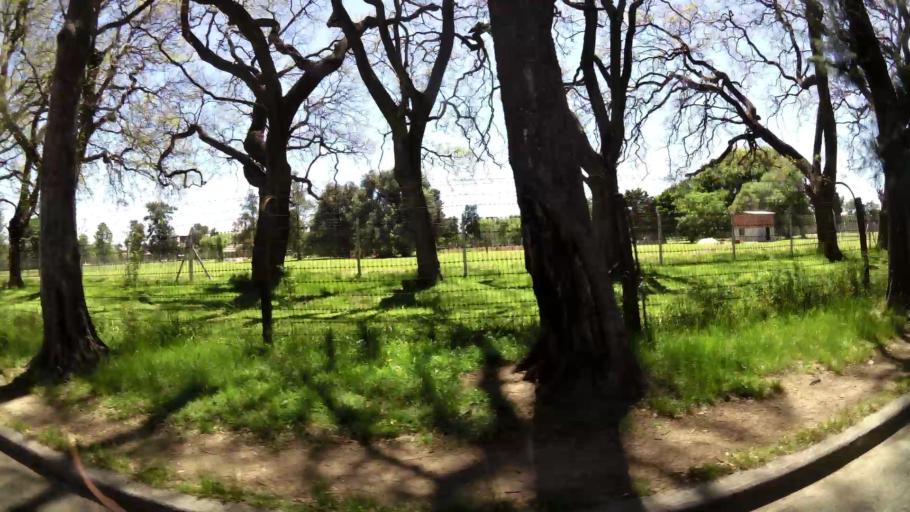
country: AR
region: Buenos Aires
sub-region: Partido de San Isidro
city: San Isidro
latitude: -34.5066
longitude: -58.5417
